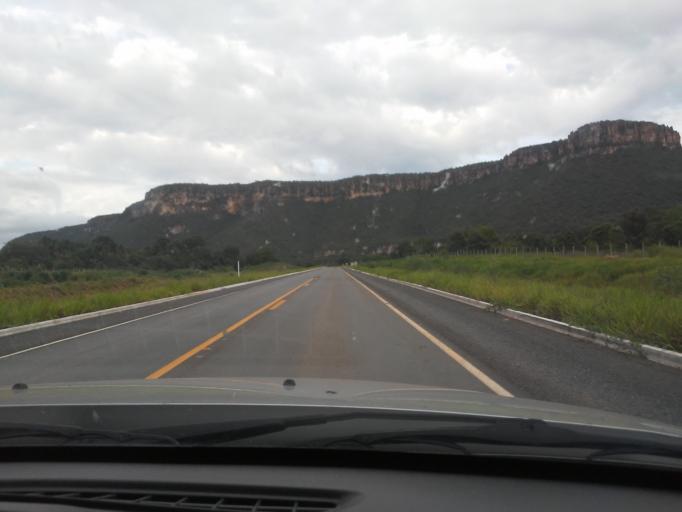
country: BR
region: Tocantins
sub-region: Taguatinga
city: Taguatinga
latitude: -12.3867
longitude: -46.4156
